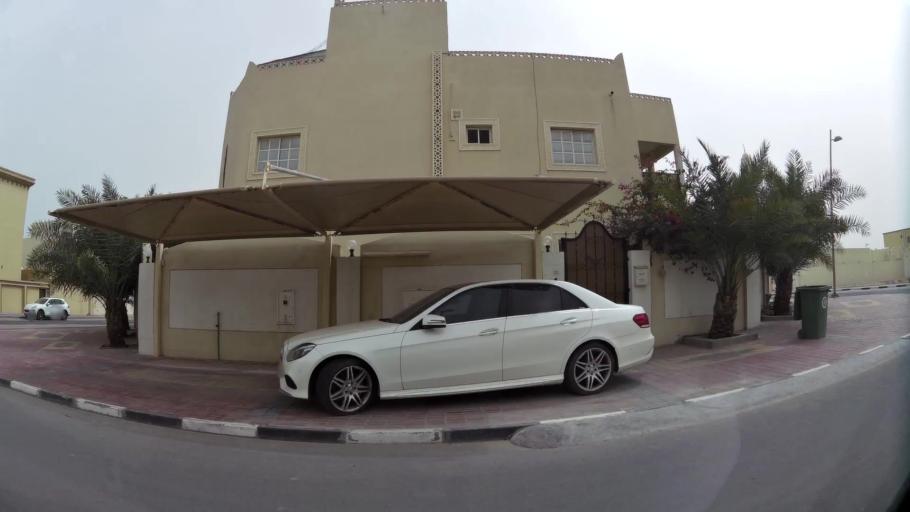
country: QA
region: Baladiyat ad Dawhah
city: Doha
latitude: 25.2317
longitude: 51.5389
